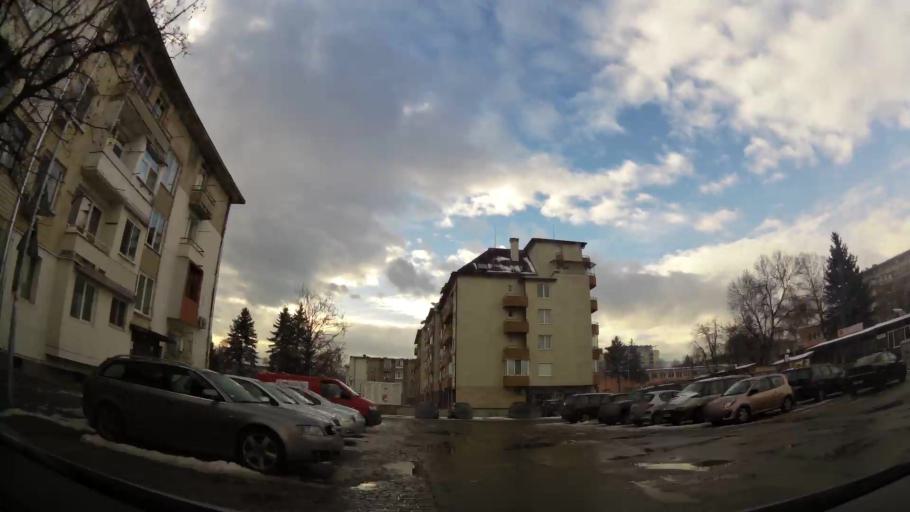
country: BG
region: Sofia-Capital
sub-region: Stolichna Obshtina
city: Sofia
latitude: 42.7046
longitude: 23.2785
